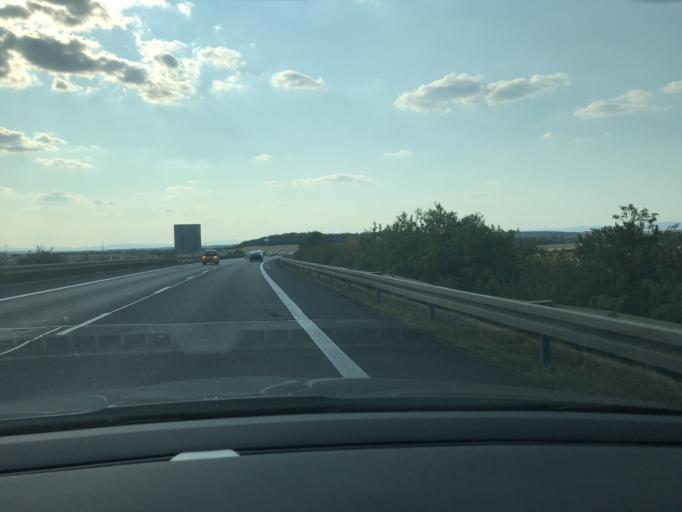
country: CZ
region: Ustecky
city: Lenesice
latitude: 50.3500
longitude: 13.7585
